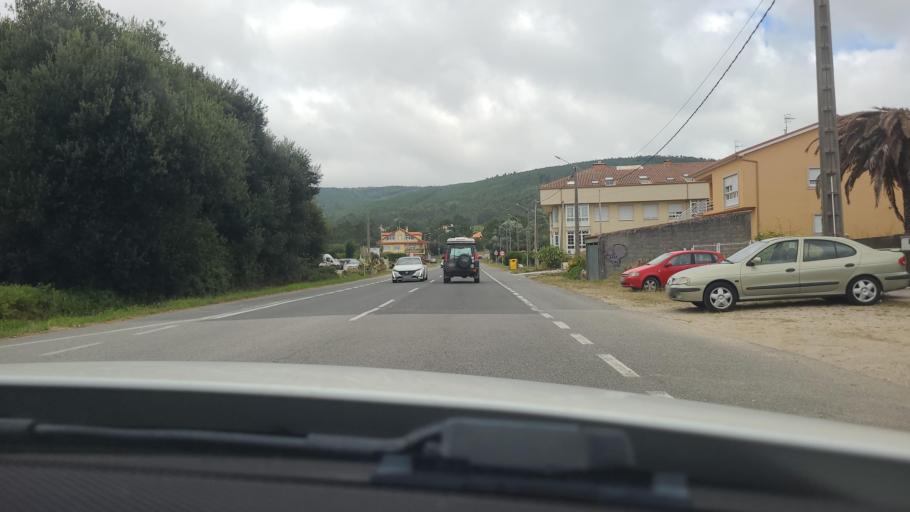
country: ES
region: Galicia
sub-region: Provincia da Coruna
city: Fisterra
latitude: 42.9256
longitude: -9.2605
